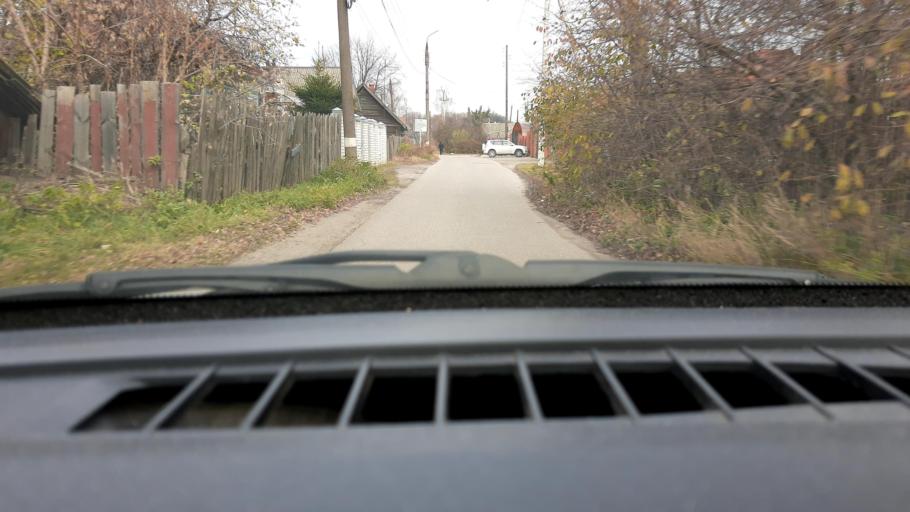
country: RU
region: Nizjnij Novgorod
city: Gorodets
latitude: 56.6380
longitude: 43.4703
